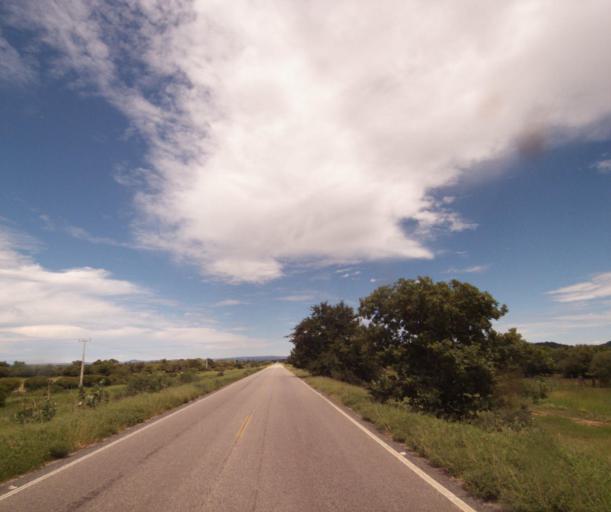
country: BR
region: Bahia
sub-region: Guanambi
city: Guanambi
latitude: -14.2296
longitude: -42.9274
